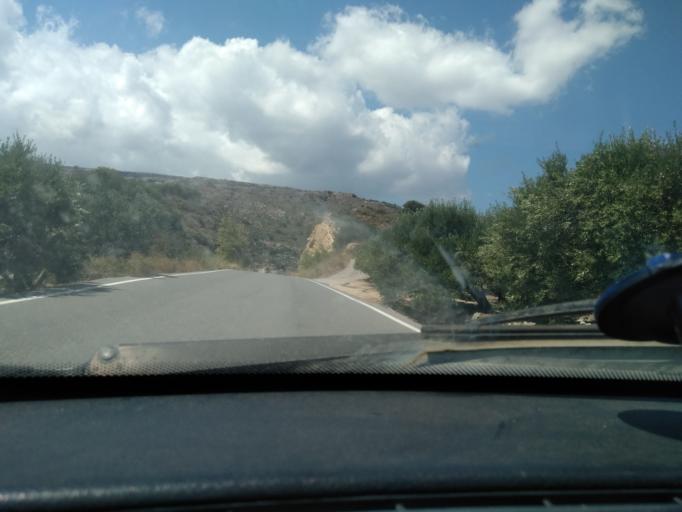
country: GR
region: Crete
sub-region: Nomos Lasithiou
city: Siteia
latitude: 35.1295
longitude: 26.0717
